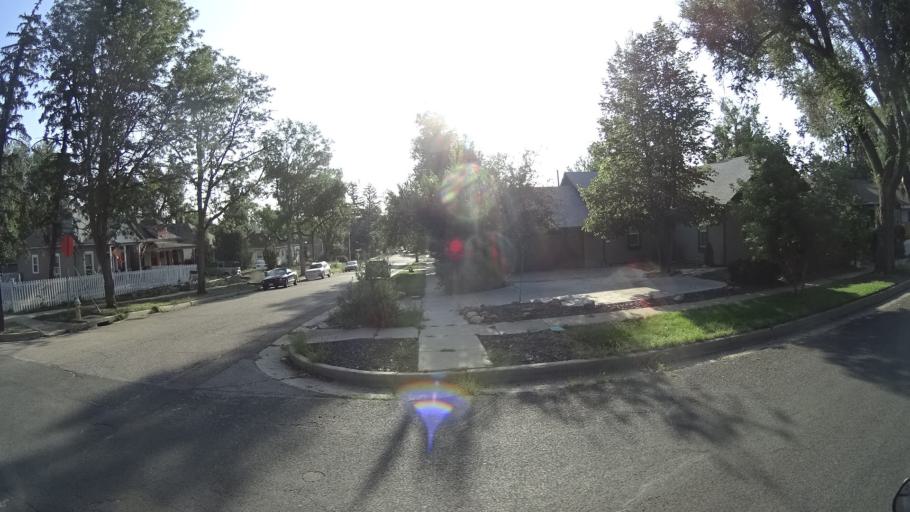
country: US
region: Colorado
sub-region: El Paso County
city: Colorado Springs
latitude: 38.8408
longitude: -104.8337
